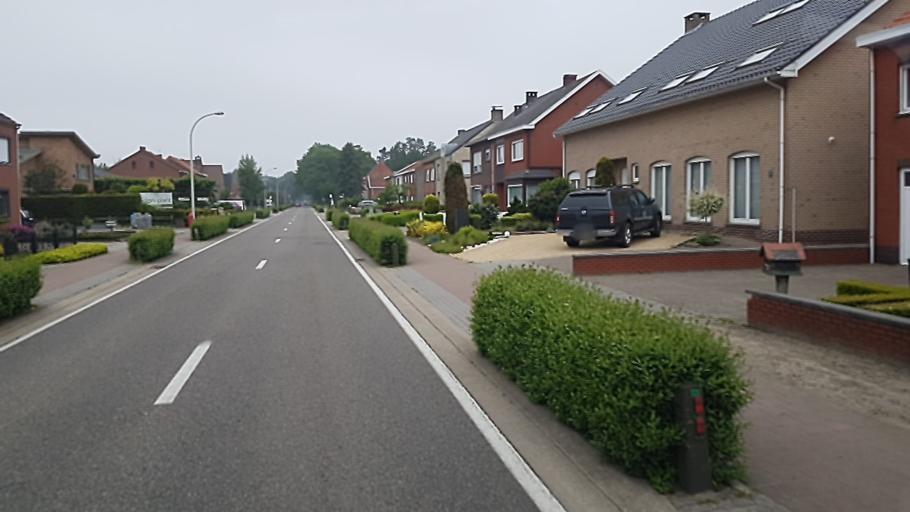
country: BE
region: Flanders
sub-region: Provincie Antwerpen
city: Brecht
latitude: 51.3335
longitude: 4.6685
